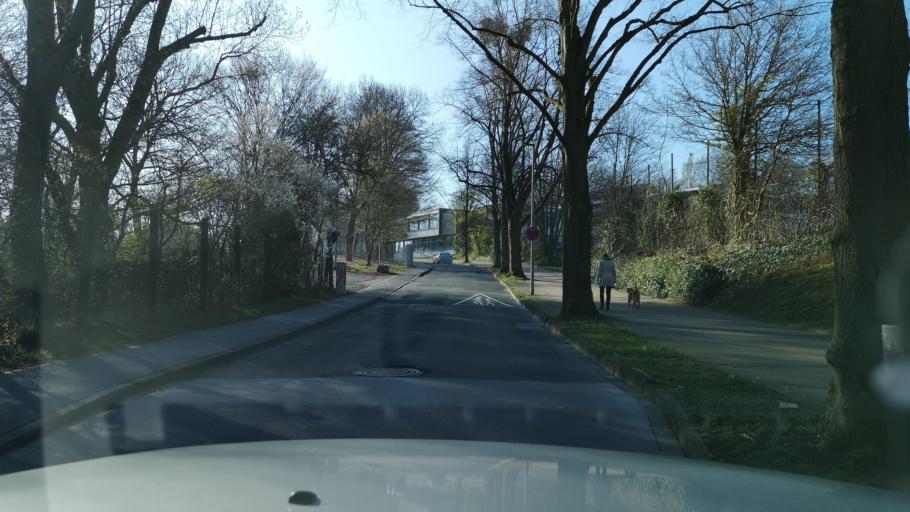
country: DE
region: North Rhine-Westphalia
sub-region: Regierungsbezirk Arnsberg
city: Menden
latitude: 51.4328
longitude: 7.7929
